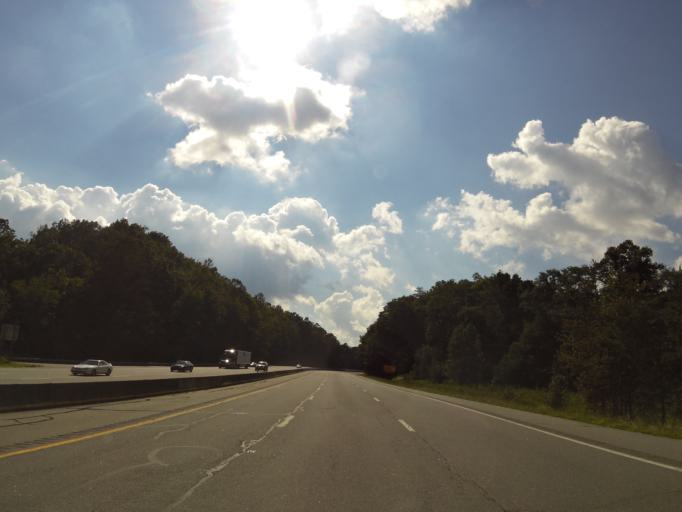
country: US
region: North Carolina
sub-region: Buncombe County
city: Black Mountain
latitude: 35.6238
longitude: -82.1974
